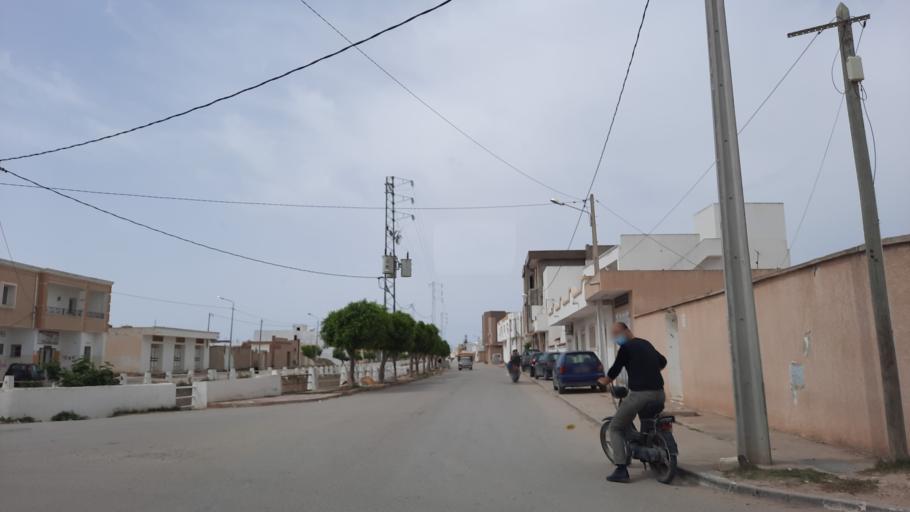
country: TN
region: Al Mahdiyah
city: El Jem
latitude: 35.3019
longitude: 10.7050
